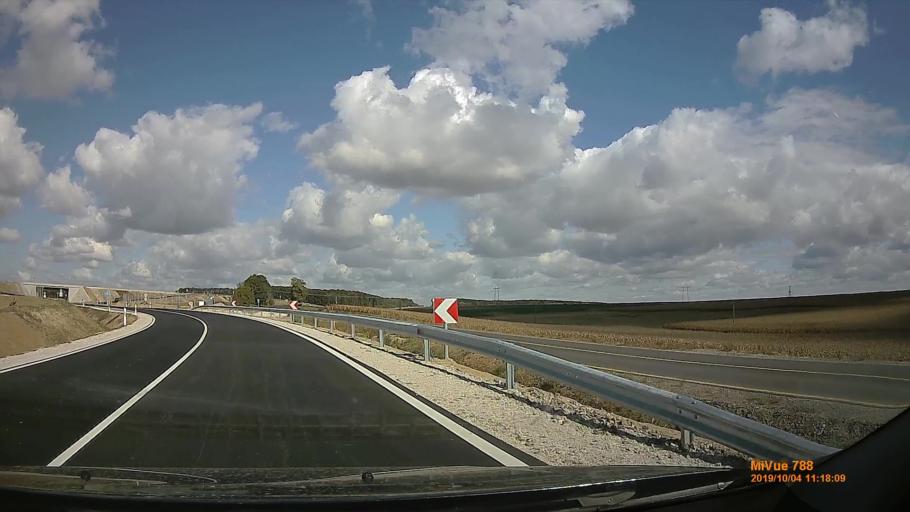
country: HU
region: Somogy
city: Kaposvar
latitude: 46.4691
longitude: 17.8034
